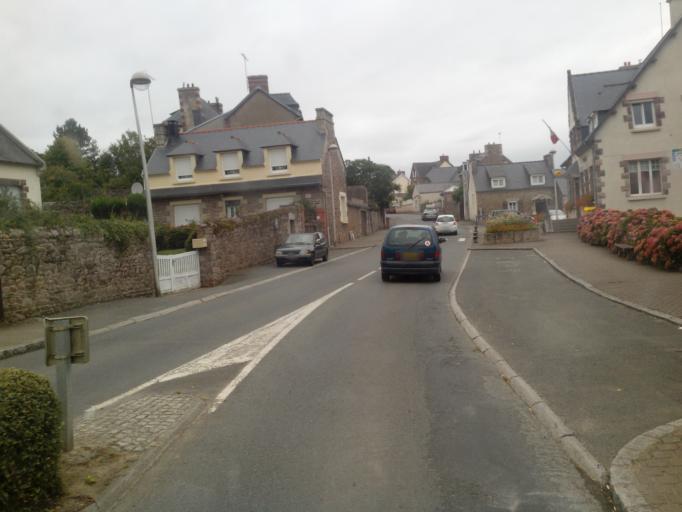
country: FR
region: Brittany
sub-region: Departement des Cotes-d'Armor
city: Paimpol
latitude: 48.7693
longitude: -3.0258
